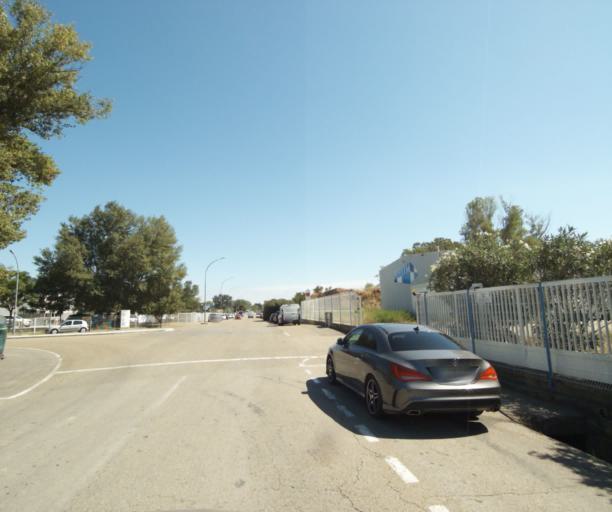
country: FR
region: Languedoc-Roussillon
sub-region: Departement du Gard
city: Rodilhan
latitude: 43.8363
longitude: 4.4215
